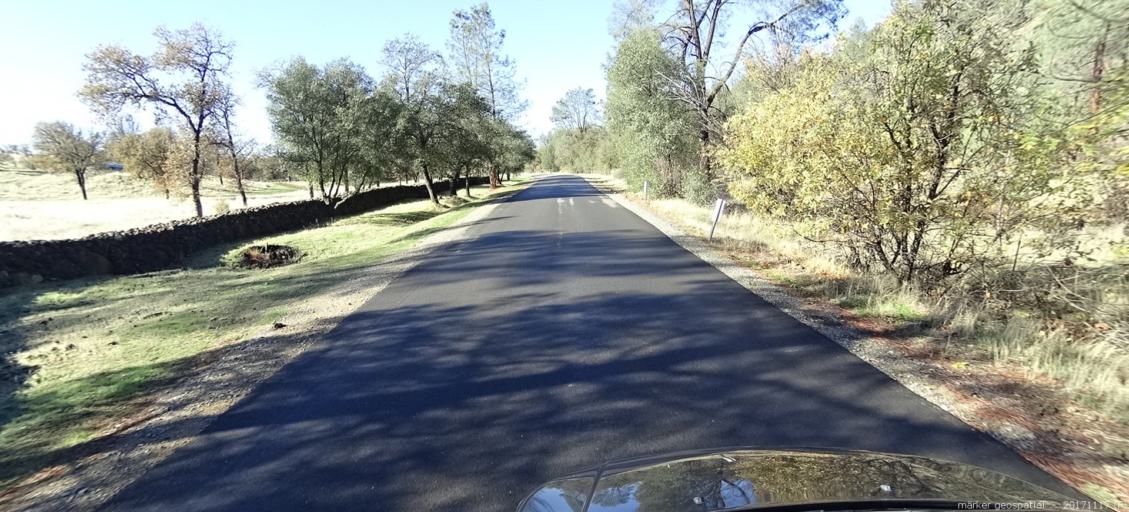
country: US
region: California
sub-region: Shasta County
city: Cottonwood
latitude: 40.4414
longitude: -122.1428
